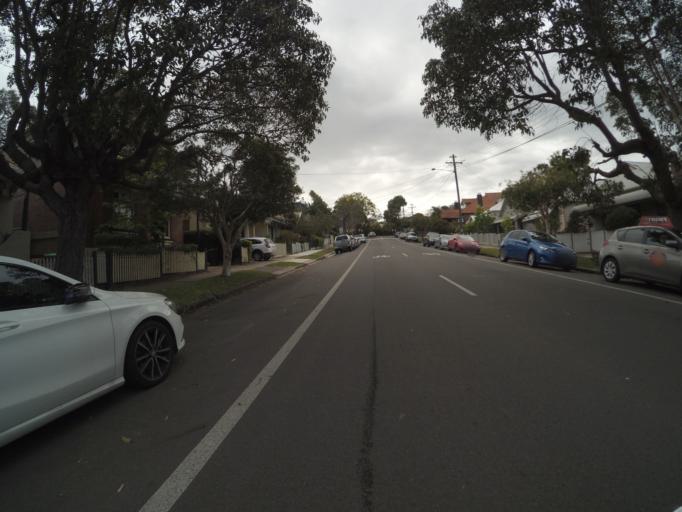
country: AU
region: New South Wales
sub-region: Canada Bay
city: Drummoyne
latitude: -33.8514
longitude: 151.1560
